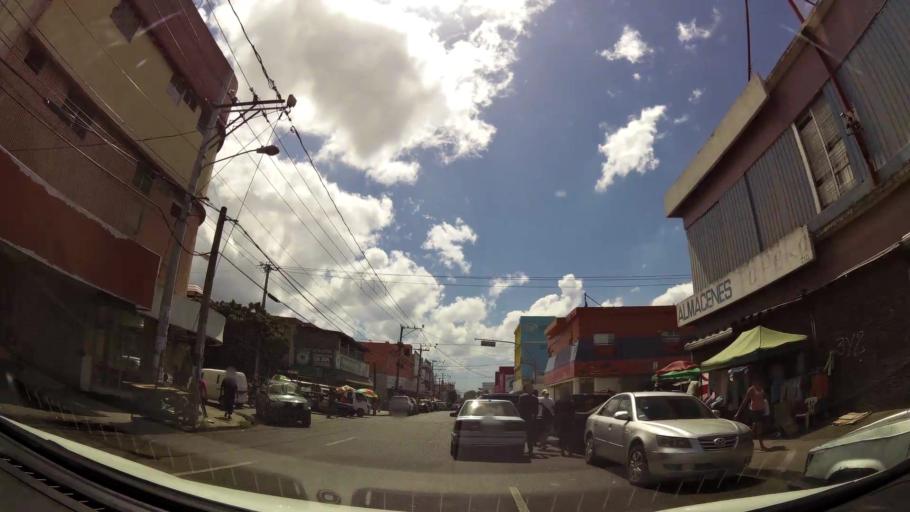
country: DO
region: Nacional
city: San Carlos
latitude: 18.4895
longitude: -69.8964
